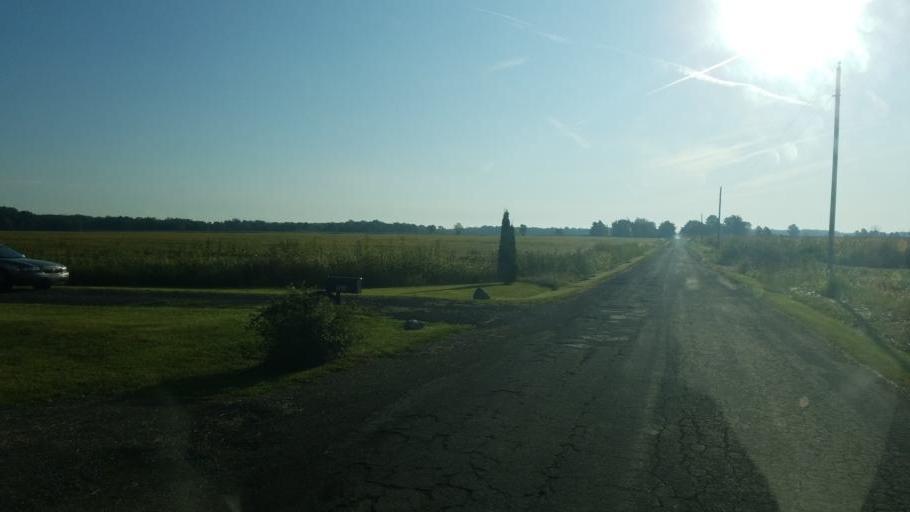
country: US
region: Ohio
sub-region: Morrow County
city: Mount Gilead
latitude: 40.6162
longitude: -82.9265
